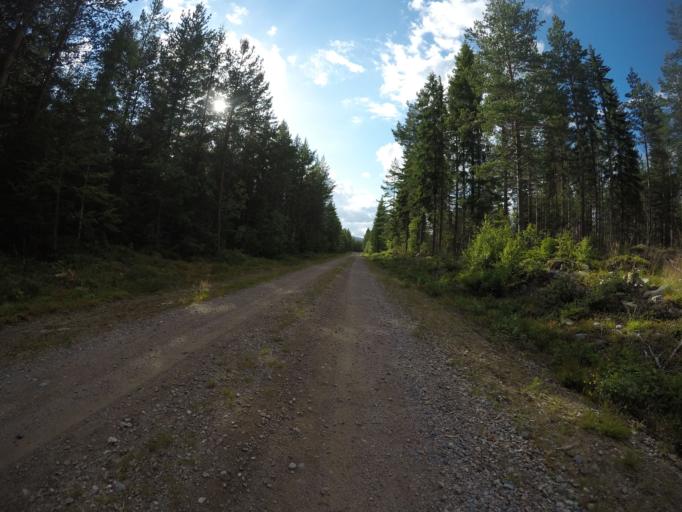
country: SE
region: OErebro
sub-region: Hallefors Kommun
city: Haellefors
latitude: 59.9743
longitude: 14.5588
